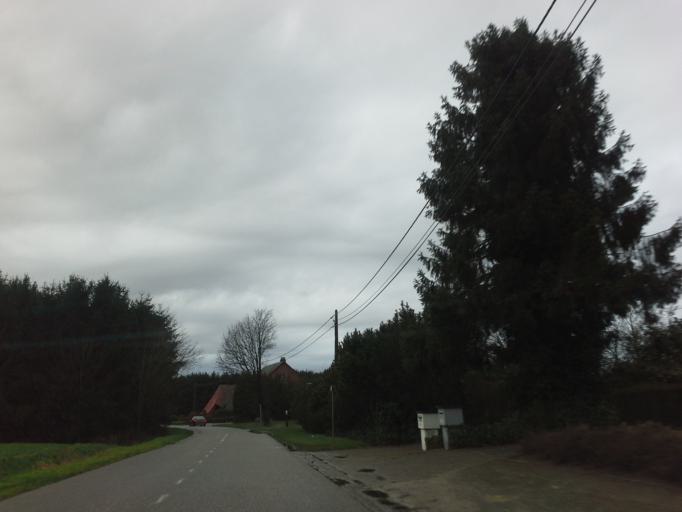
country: BE
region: Flanders
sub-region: Provincie Antwerpen
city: Meerhout
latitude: 51.1211
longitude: 5.0706
